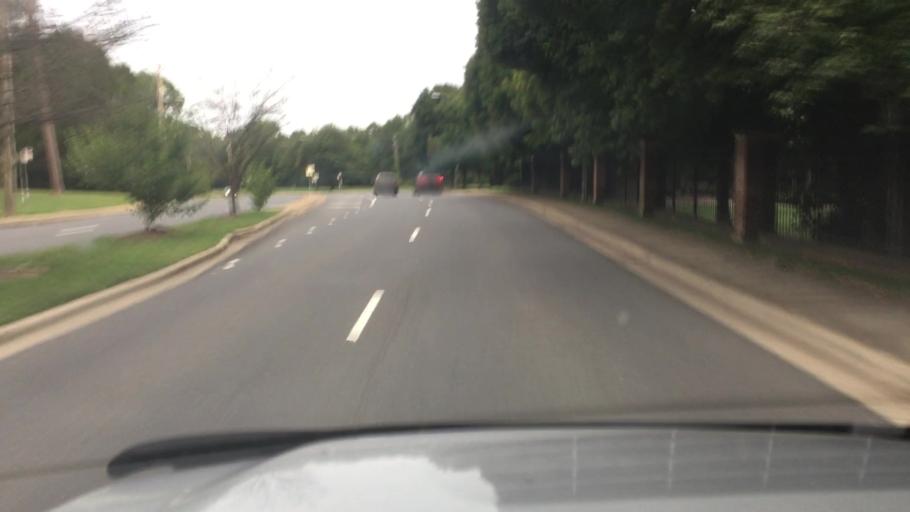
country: US
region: North Carolina
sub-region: Mecklenburg County
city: Pineville
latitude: 35.1043
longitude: -80.8320
